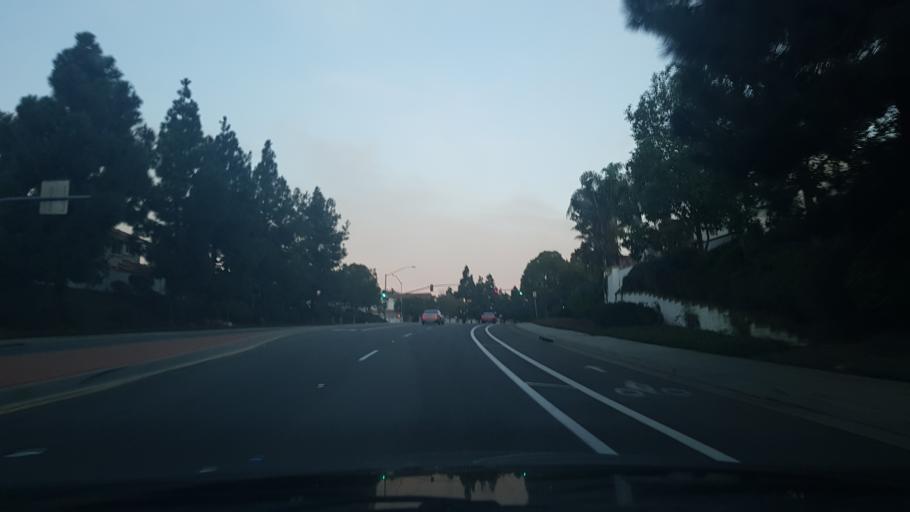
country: US
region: California
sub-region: San Diego County
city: Del Mar
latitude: 32.9124
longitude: -117.1992
